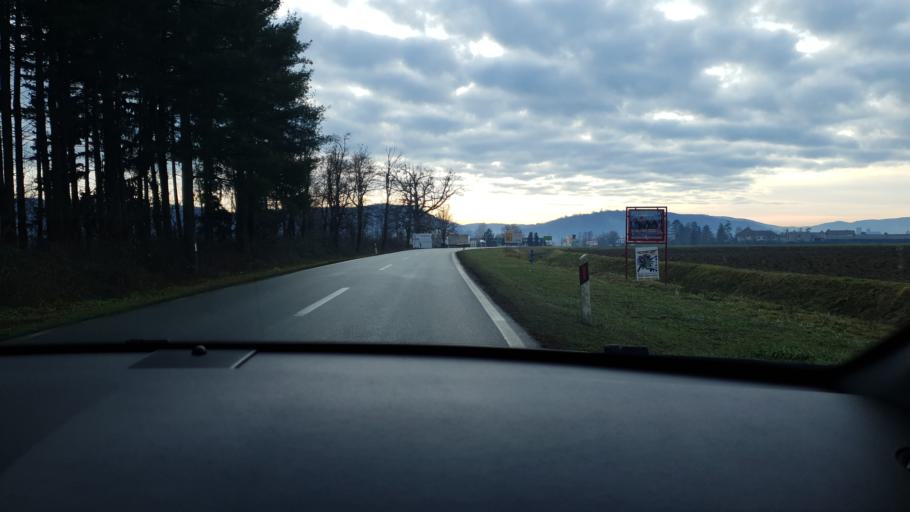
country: HR
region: Pozesko-Slavonska
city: Vidovci
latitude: 45.3461
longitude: 17.7178
